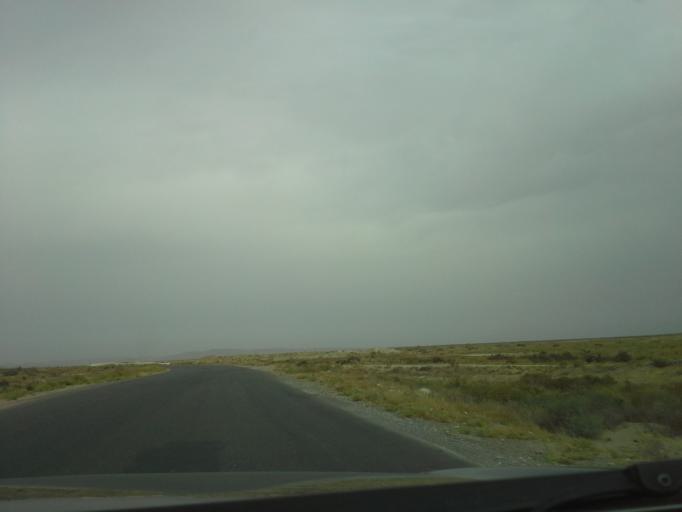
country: TM
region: Lebap
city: Atamyrat
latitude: 37.7288
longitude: 65.5070
